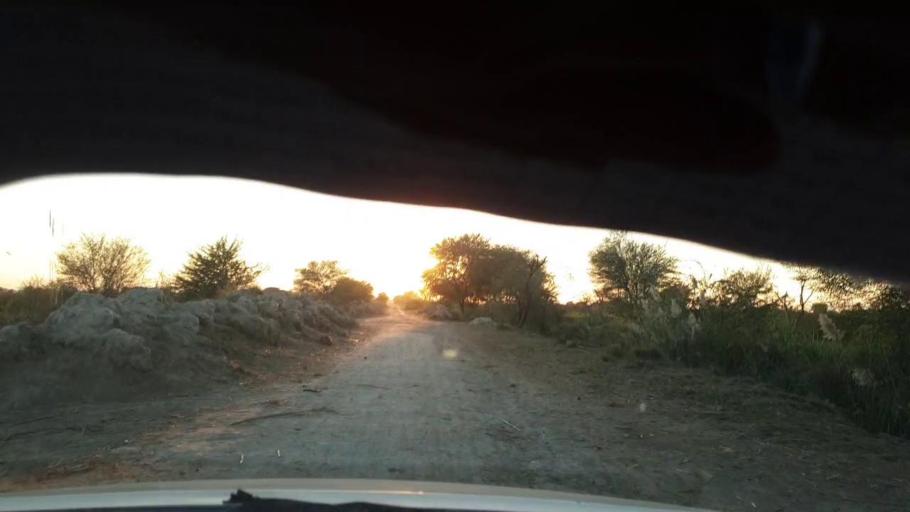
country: PK
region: Sindh
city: Jhol
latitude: 25.8955
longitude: 68.8816
